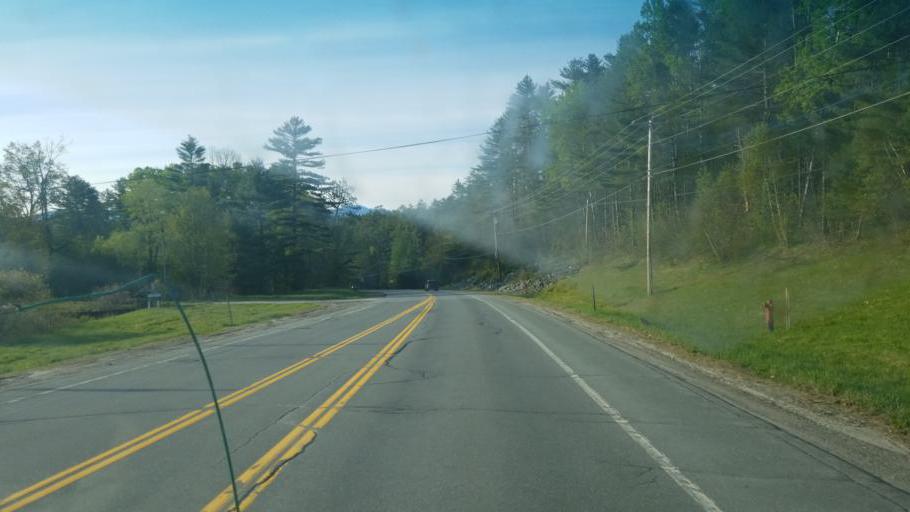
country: US
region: New Hampshire
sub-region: Grafton County
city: Littleton
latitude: 44.3225
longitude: -71.8040
